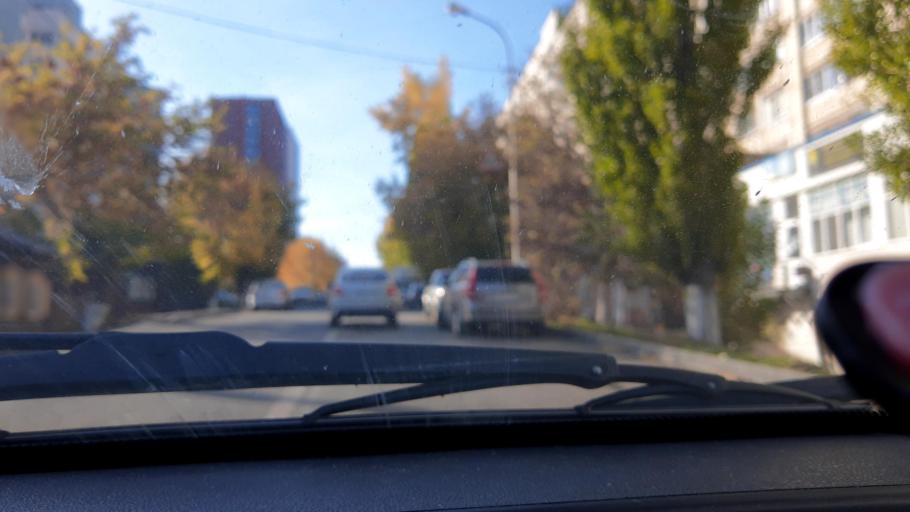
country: RU
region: Bashkortostan
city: Ufa
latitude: 54.7376
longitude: 55.9338
